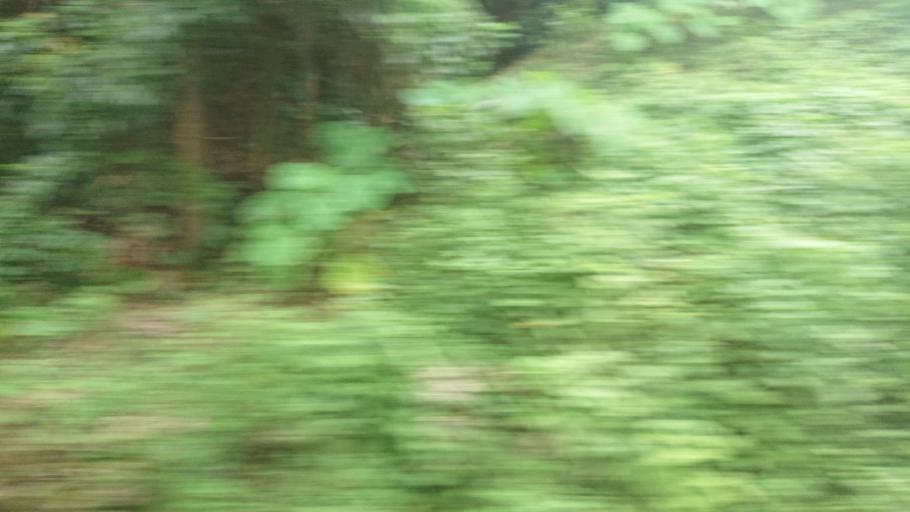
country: TW
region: Taiwan
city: Lugu
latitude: 23.8331
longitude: 120.7558
